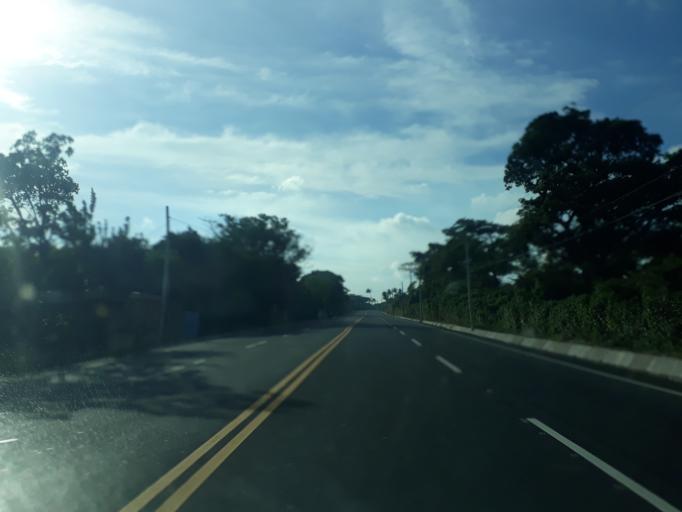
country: NI
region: Carazo
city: Diriamba
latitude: 11.9159
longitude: -86.2721
